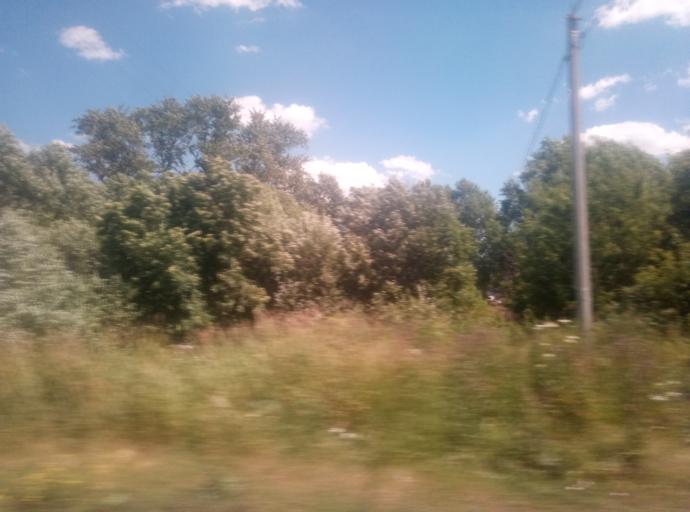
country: RU
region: Tula
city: Kireyevsk
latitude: 53.9632
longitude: 37.9374
